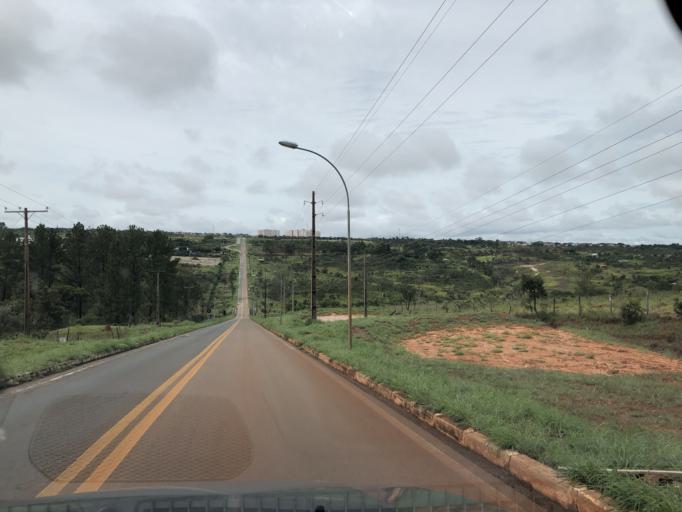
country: BR
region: Federal District
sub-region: Brasilia
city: Brasilia
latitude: -15.7662
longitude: -48.1282
